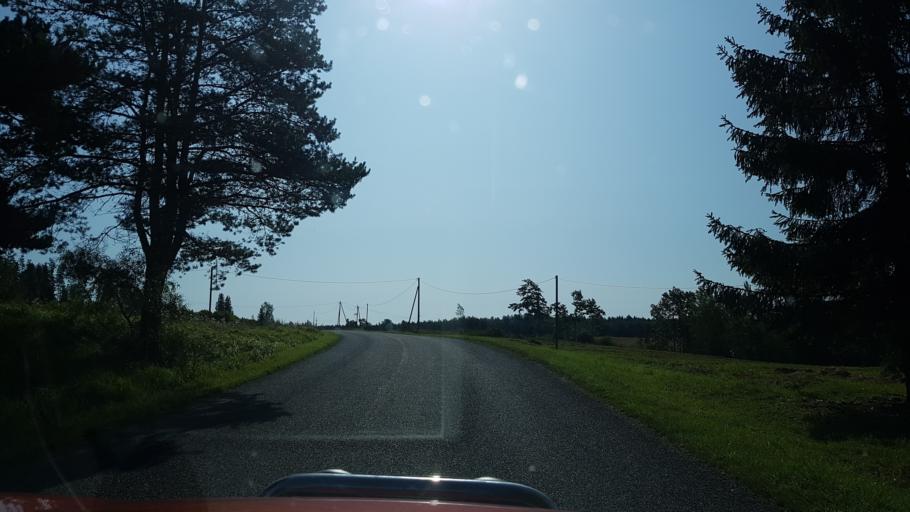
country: EE
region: Vorumaa
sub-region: Voru linn
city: Voru
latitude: 57.7282
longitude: 26.8486
